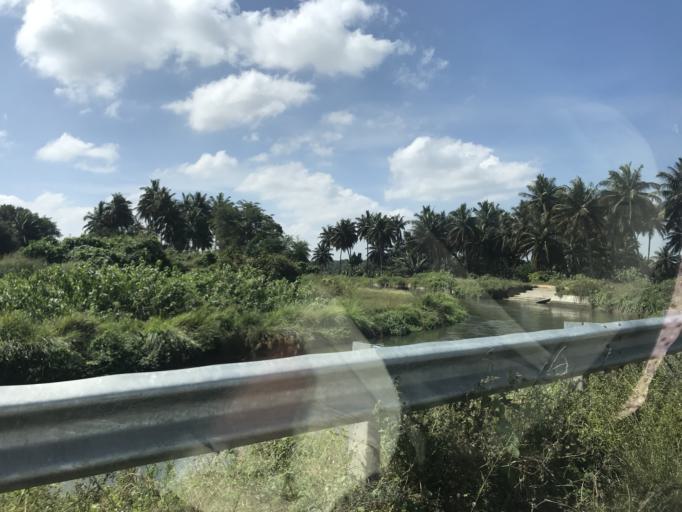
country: IN
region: Karnataka
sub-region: Mandya
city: Shrirangapattana
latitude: 12.4195
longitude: 76.6591
